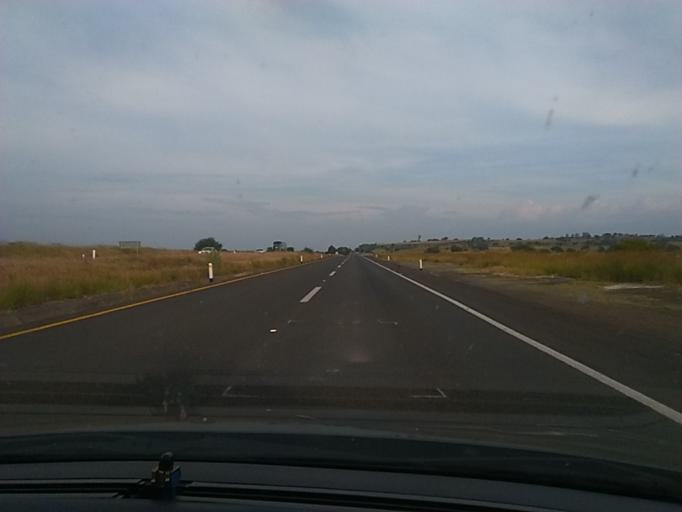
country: MX
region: Michoacan
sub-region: Alvaro Obregon
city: Lazaro Cardenas (La Purisima)
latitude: 19.8926
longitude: -101.0649
